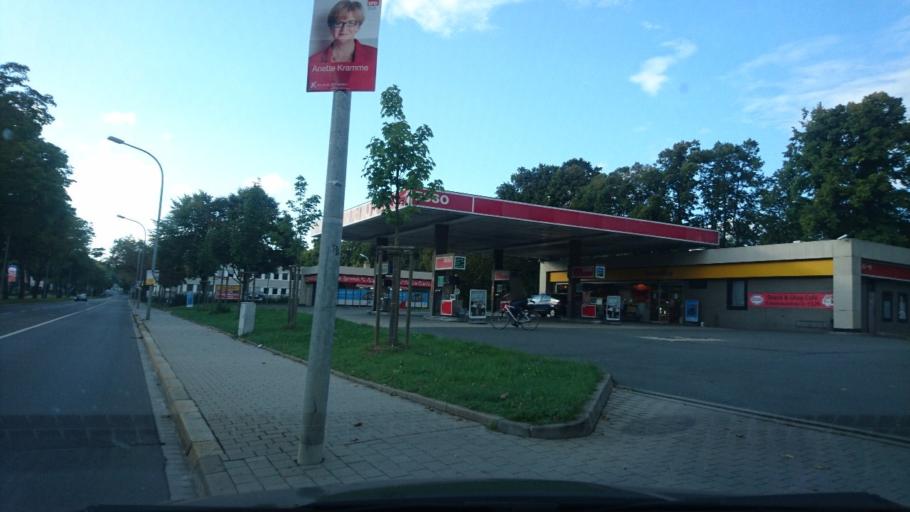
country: DE
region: Bavaria
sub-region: Upper Franconia
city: Bayreuth
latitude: 49.9473
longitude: 11.5681
